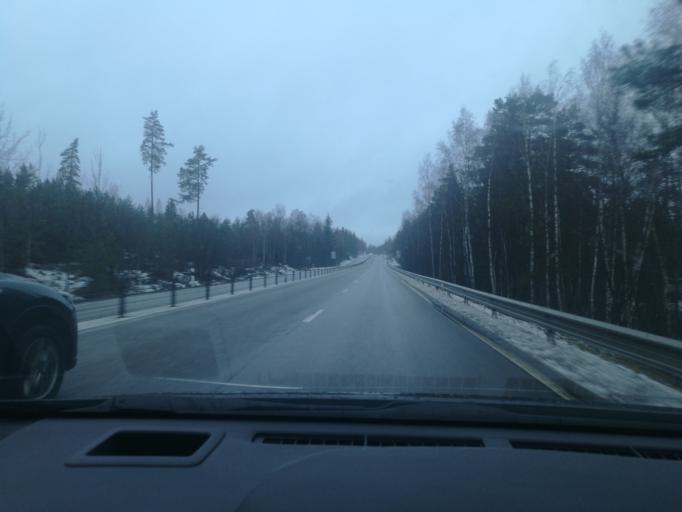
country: SE
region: OEstergoetland
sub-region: Norrkopings Kommun
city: Jursla
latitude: 58.7559
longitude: 16.1750
